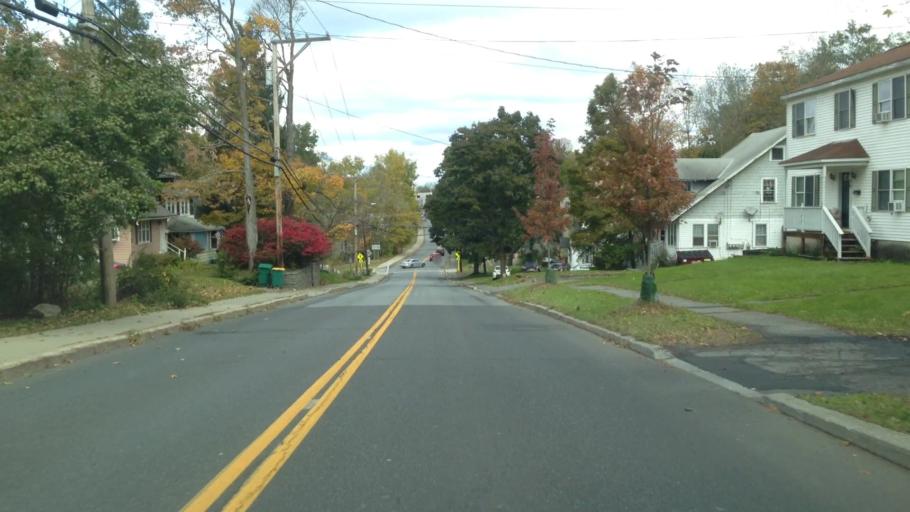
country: US
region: New York
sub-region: Ulster County
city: New Paltz
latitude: 41.7439
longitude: -74.0884
